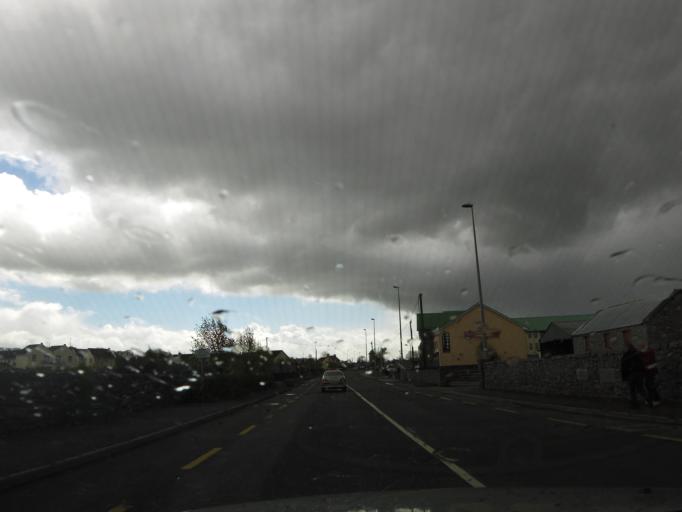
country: IE
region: Connaught
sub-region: County Galway
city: Claregalway
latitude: 53.3457
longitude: -8.9424
